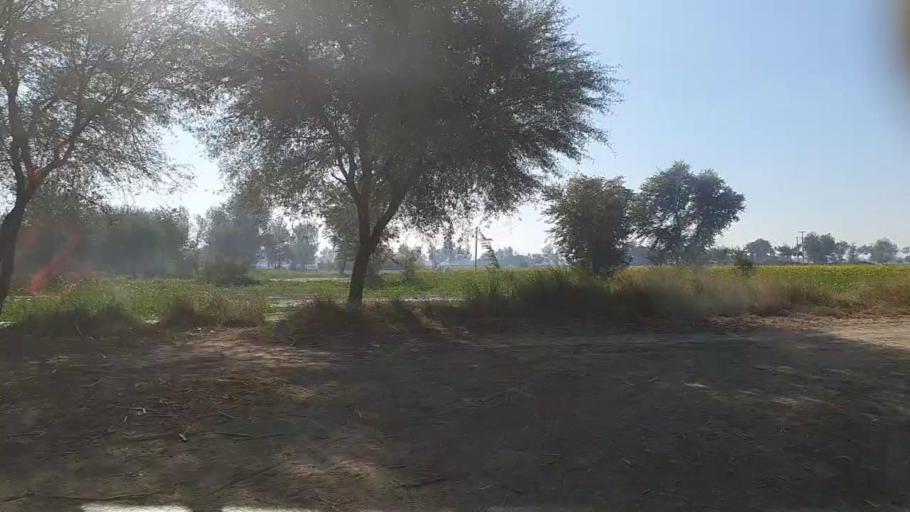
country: PK
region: Sindh
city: Khairpur
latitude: 28.0022
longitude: 69.6472
